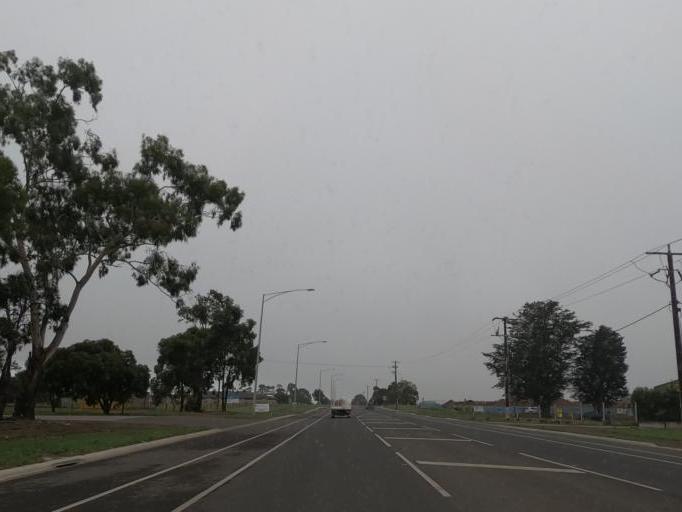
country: AU
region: Victoria
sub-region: Ballarat North
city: Newington
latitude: -37.5634
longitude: 143.8116
